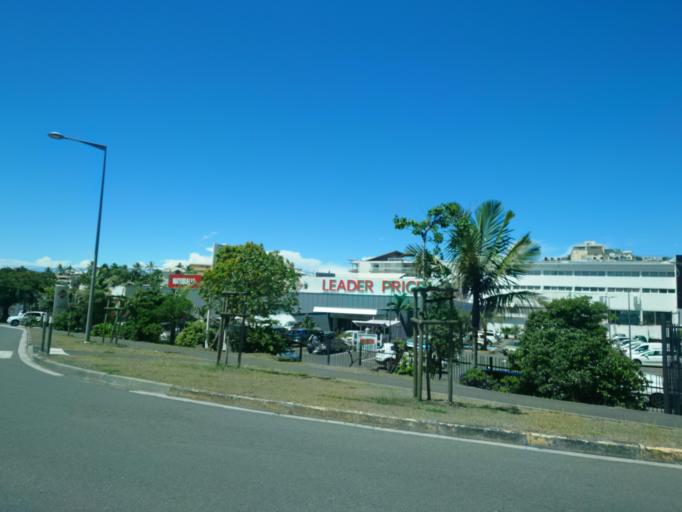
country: NC
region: South Province
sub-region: Noumea
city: Noumea
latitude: -22.2676
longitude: 166.4633
